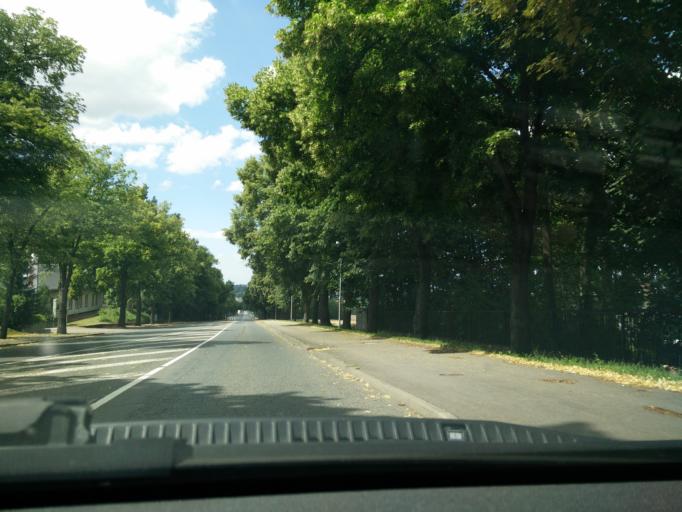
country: DE
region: Saxony
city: Hartmannsdorf
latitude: 50.8818
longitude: 12.8145
